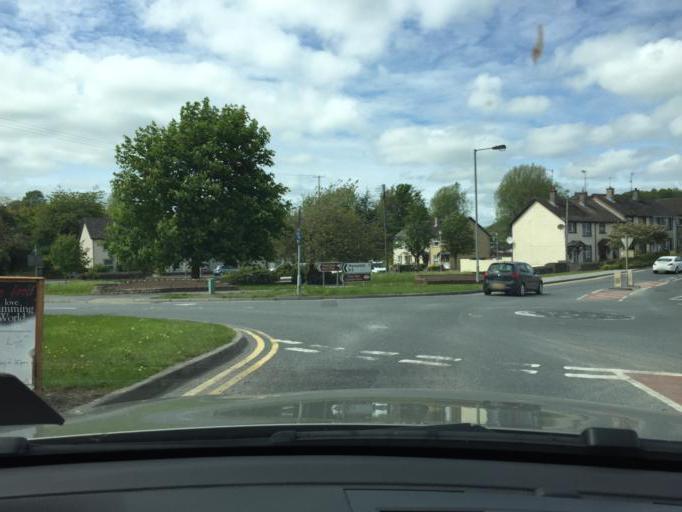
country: GB
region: Northern Ireland
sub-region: Armagh District
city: Tandragee
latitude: 54.3499
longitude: -6.4109
